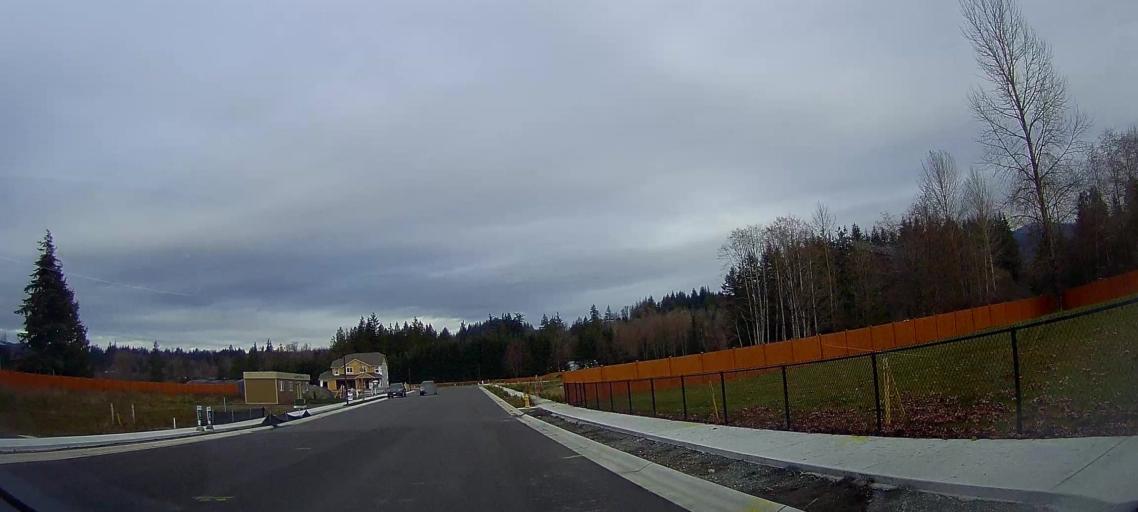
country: US
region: Washington
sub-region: Skagit County
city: Sedro-Woolley
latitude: 48.5150
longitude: -122.2438
